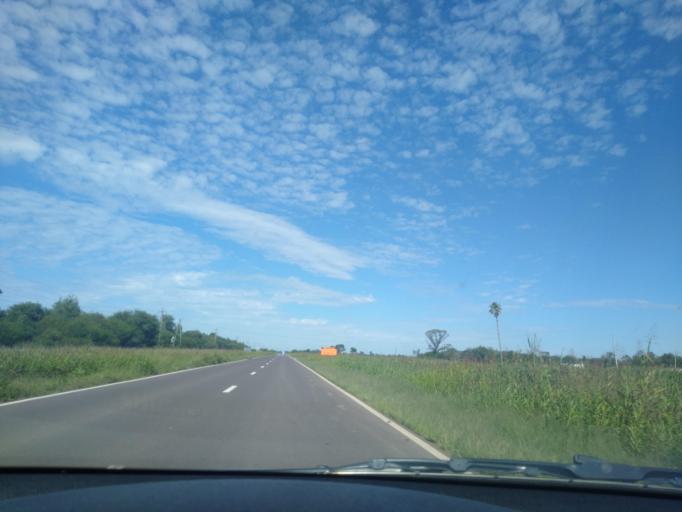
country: AR
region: Chaco
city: Presidencia Roque Saenz Pena
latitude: -26.7532
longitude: -60.3924
